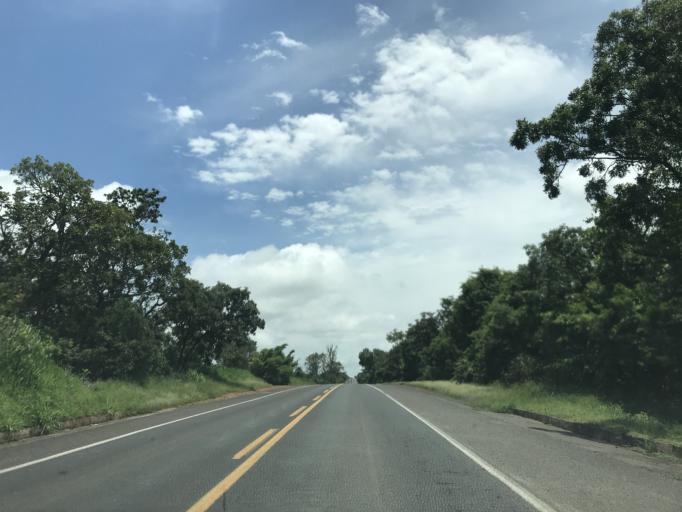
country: BR
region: Minas Gerais
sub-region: Prata
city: Prata
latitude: -19.6280
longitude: -48.9447
